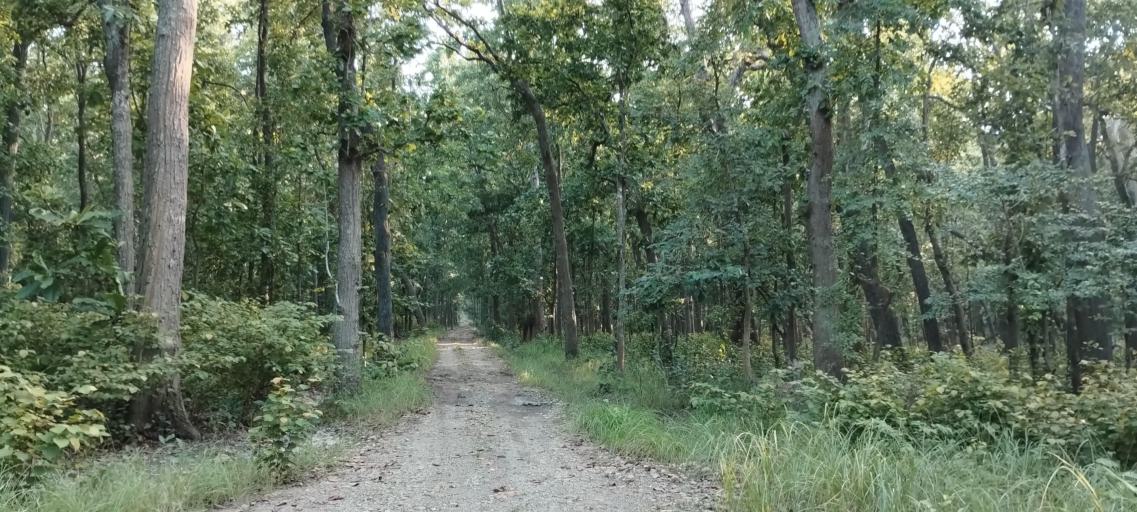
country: NP
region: Far Western
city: Tikapur
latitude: 28.5023
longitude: 81.2717
